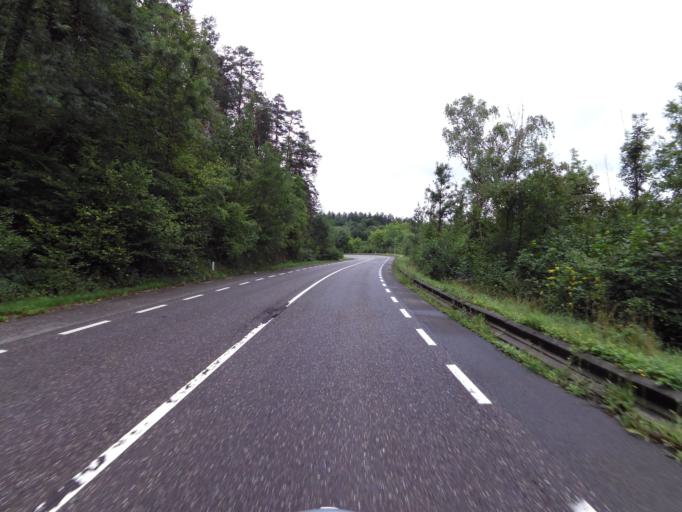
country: BE
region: Wallonia
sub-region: Province de Namur
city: Rochefort
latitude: 50.1381
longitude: 5.1851
